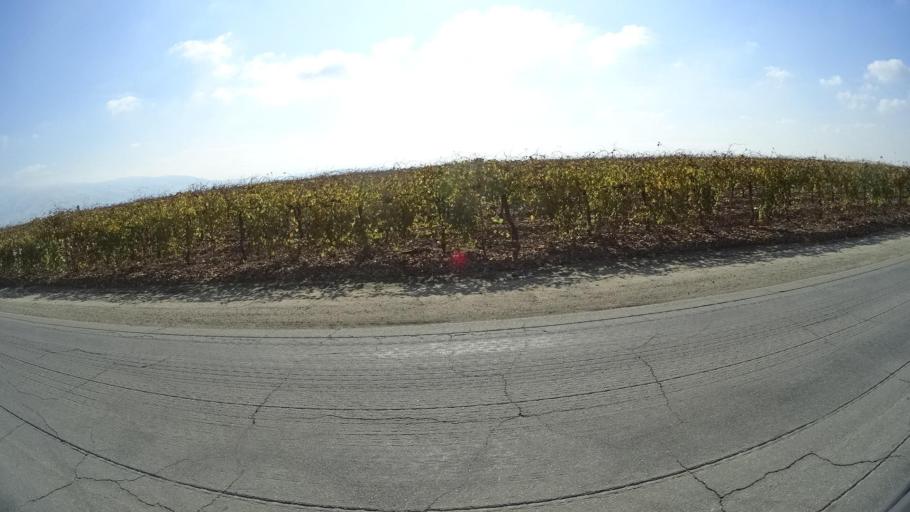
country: US
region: California
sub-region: Kern County
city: Arvin
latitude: 35.2236
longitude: -118.8539
